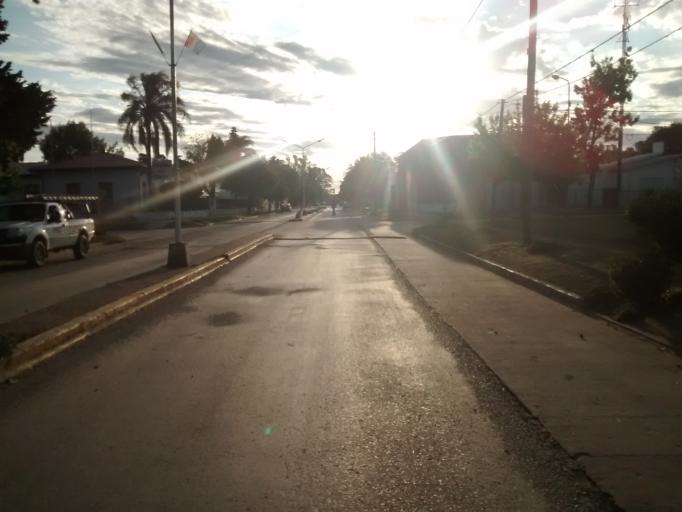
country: AR
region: Santa Fe
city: Galvez
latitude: -31.9040
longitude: -61.2756
